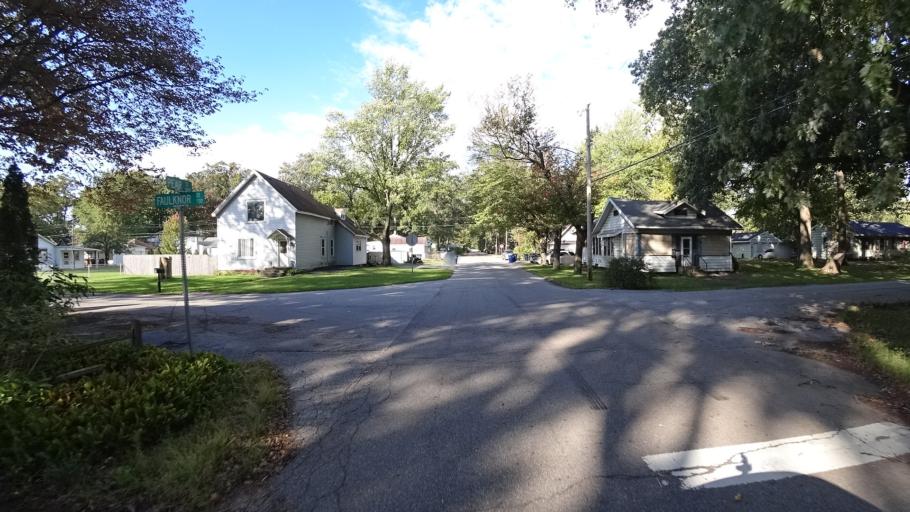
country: US
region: Indiana
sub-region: LaPorte County
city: Trail Creek
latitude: 41.7034
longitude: -86.8734
